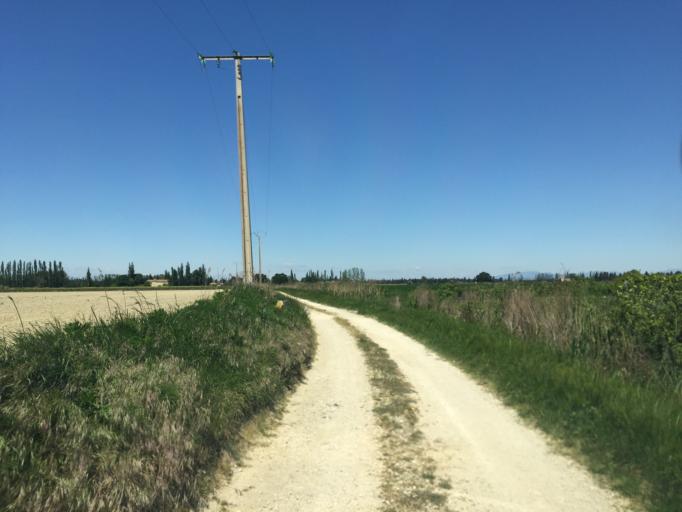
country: FR
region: Provence-Alpes-Cote d'Azur
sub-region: Departement du Vaucluse
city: Bedarrides
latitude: 44.0592
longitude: 4.9034
